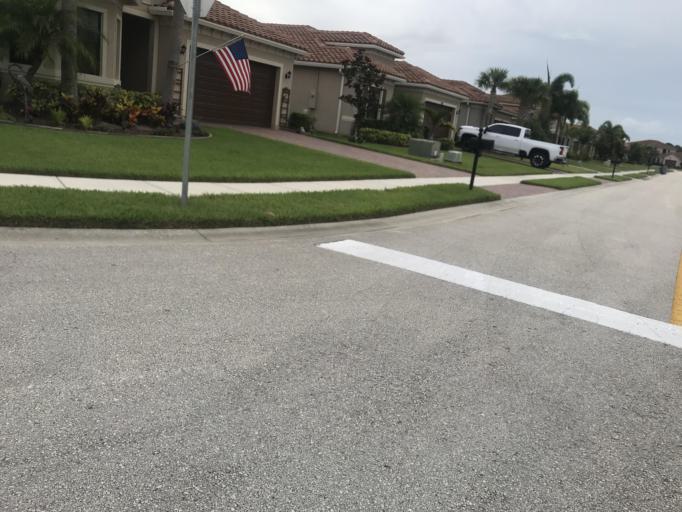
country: US
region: Florida
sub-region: Indian River County
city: Winter Beach
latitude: 27.6955
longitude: -80.4260
